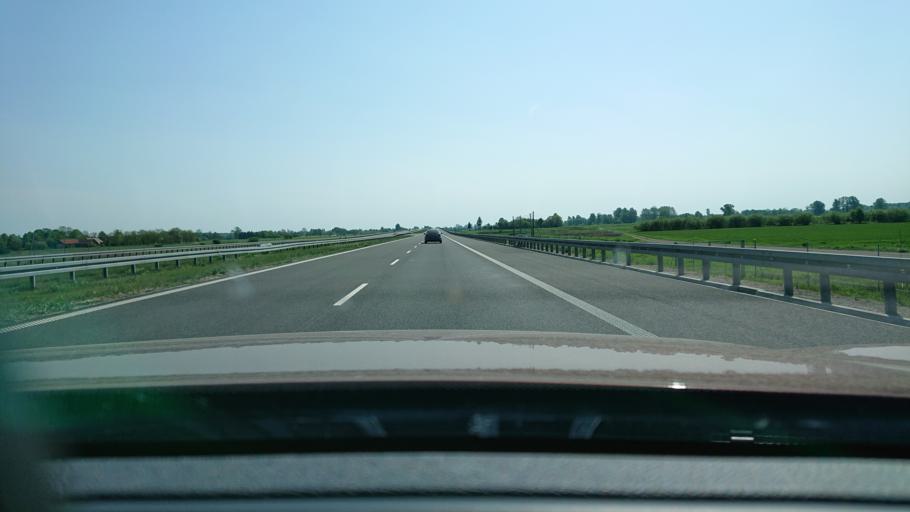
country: PL
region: Subcarpathian Voivodeship
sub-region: Powiat lancucki
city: Bialobrzegi
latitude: 50.1139
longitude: 22.3524
